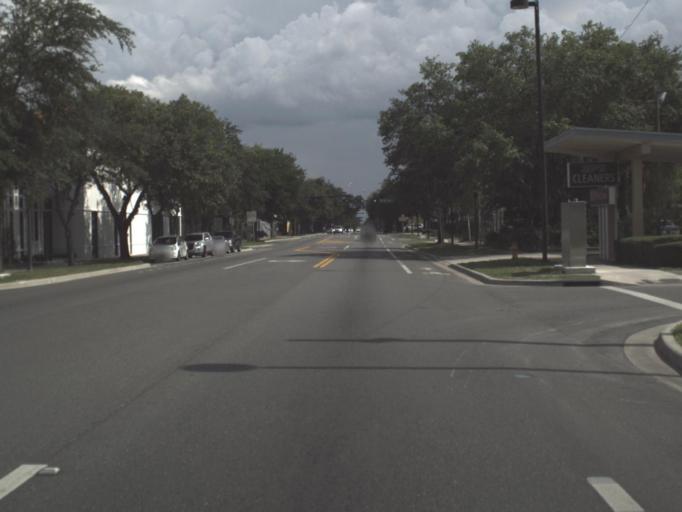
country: US
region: Florida
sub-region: Alachua County
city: Gainesville
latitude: 29.6549
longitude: -82.3251
